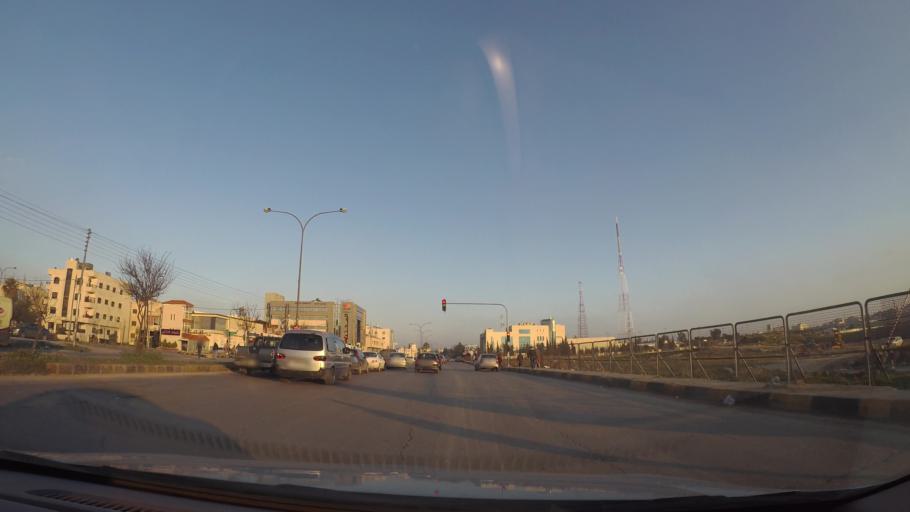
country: JO
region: Amman
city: Al Quwaysimah
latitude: 31.9083
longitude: 35.9292
